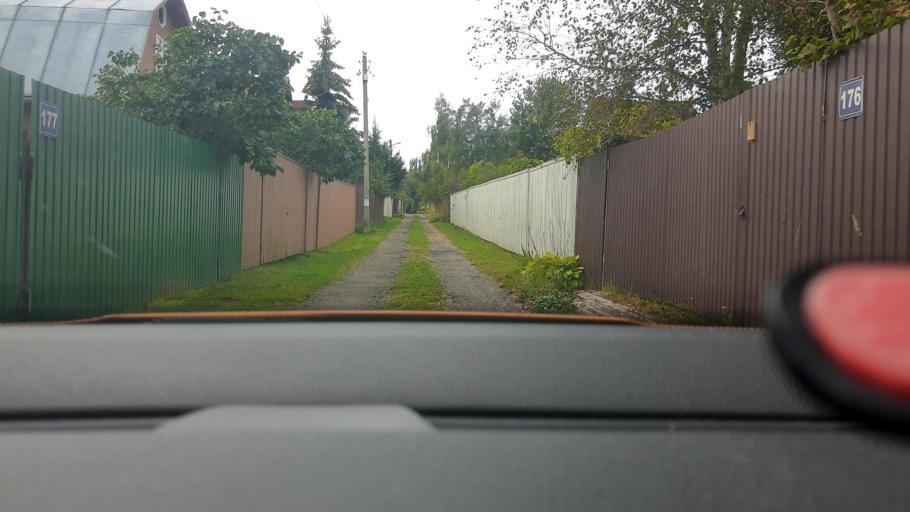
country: RU
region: Moskovskaya
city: Ashukino
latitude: 56.0900
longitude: 38.0230
